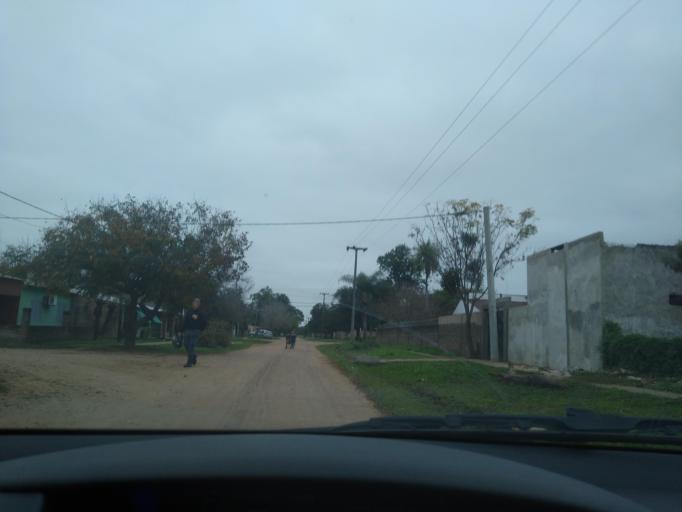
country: AR
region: Chaco
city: Colonia Benitez
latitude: -27.3323
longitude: -58.9425
